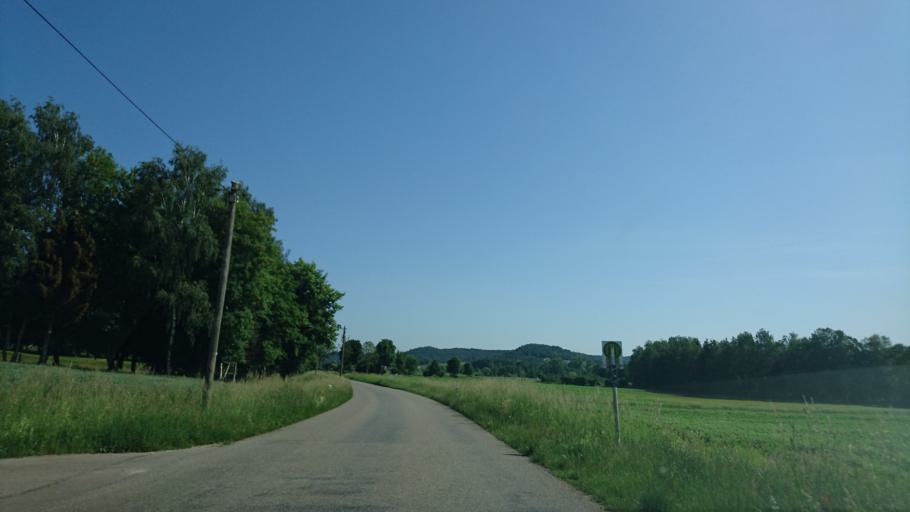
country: DE
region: Bavaria
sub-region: Swabia
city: Zusmarshausen
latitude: 48.4004
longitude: 10.5861
